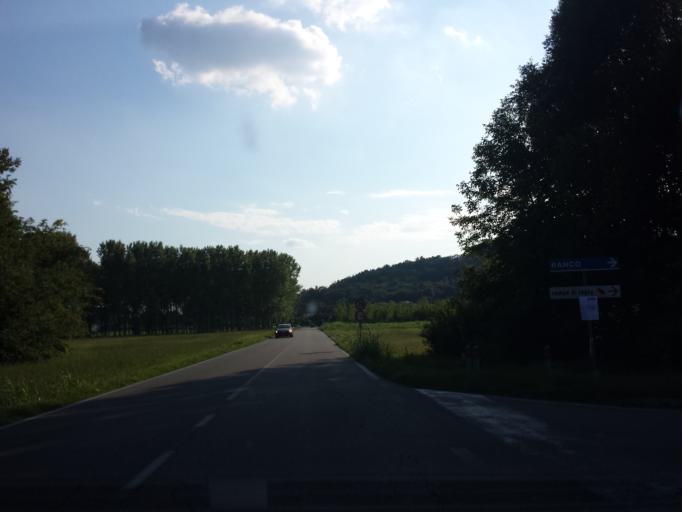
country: IT
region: Lombardy
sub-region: Provincia di Varese
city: Angera
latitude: 45.7901
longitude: 8.5978
